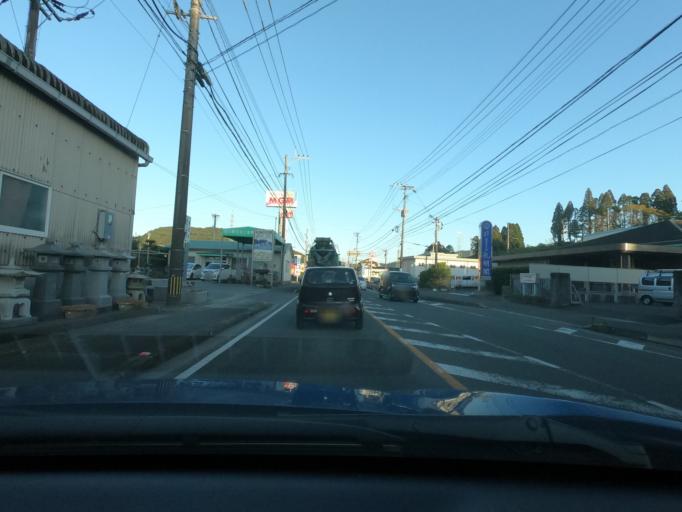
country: JP
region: Kagoshima
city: Satsumasendai
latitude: 31.8093
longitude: 130.3335
